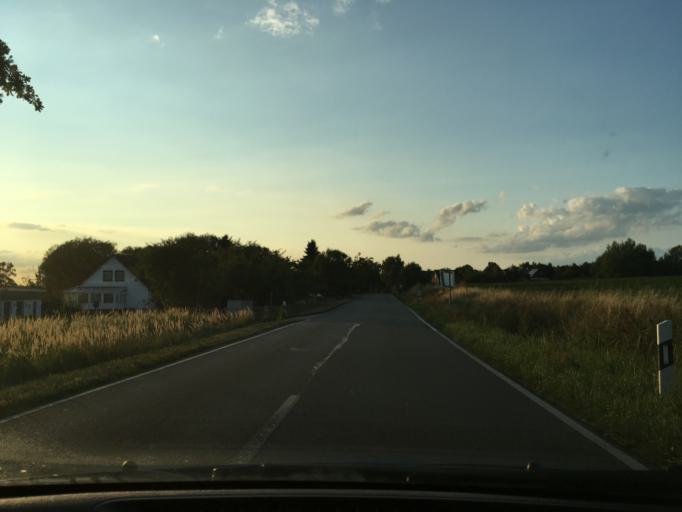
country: DE
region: Lower Saxony
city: Bleckede
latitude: 53.2517
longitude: 10.7673
